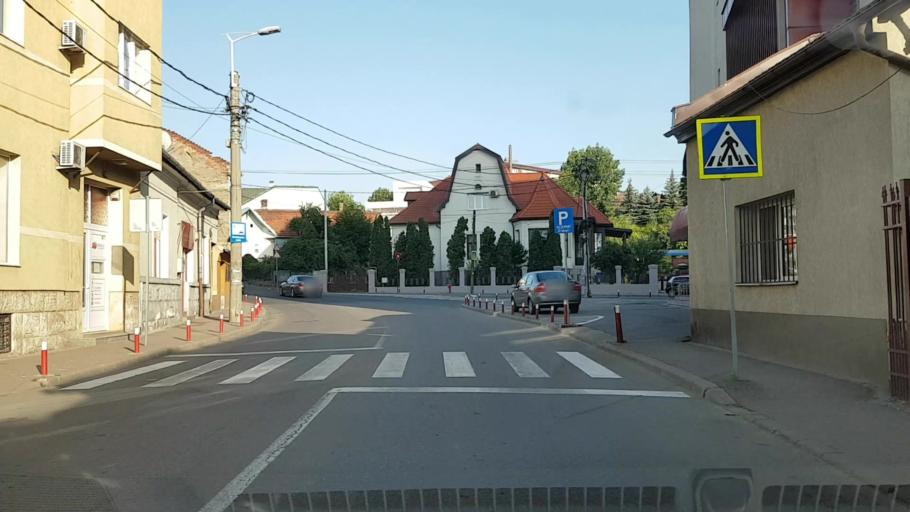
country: RO
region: Cluj
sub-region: Municipiul Cluj-Napoca
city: Cluj-Napoca
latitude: 46.7722
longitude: 23.6070
